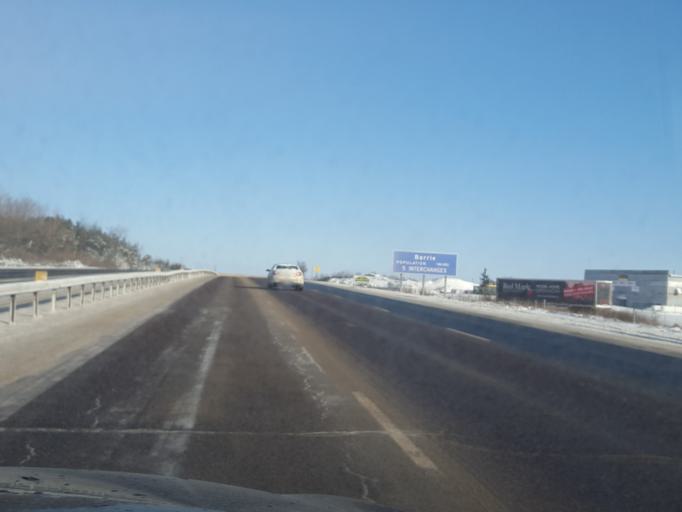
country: CA
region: Ontario
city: Innisfil
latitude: 44.3057
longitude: -79.6838
